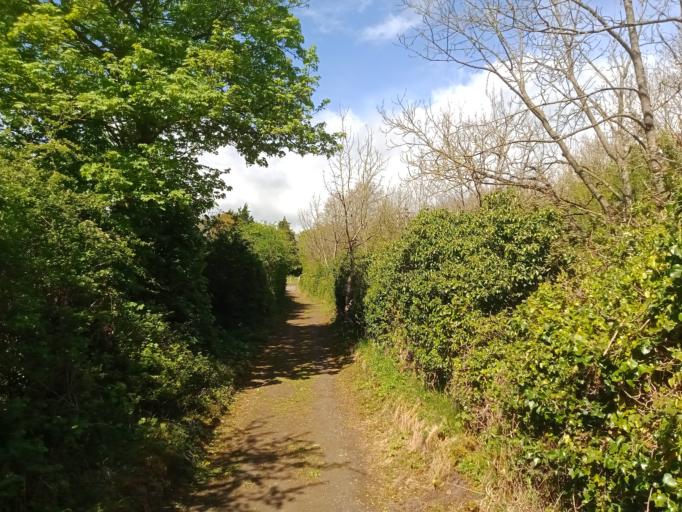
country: IE
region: Leinster
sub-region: Kilkenny
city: Kilkenny
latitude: 52.6908
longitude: -7.2614
